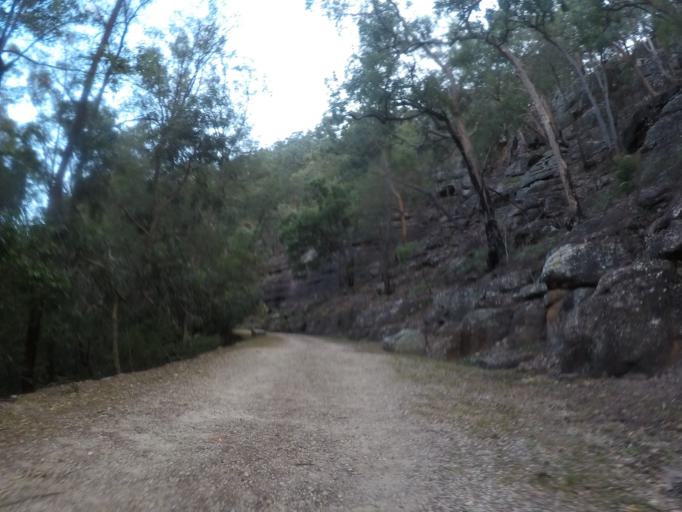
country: AU
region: New South Wales
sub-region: Hornsby Shire
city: Glenorie
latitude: -33.3734
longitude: 150.9847
